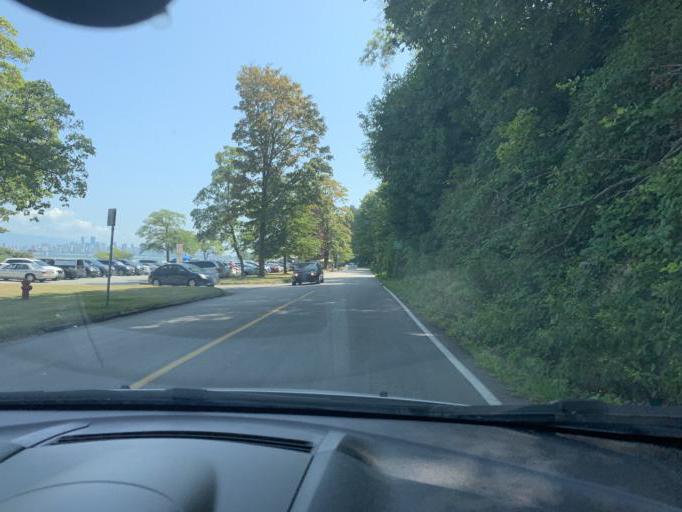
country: CA
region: British Columbia
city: West End
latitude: 49.2773
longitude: -123.2227
